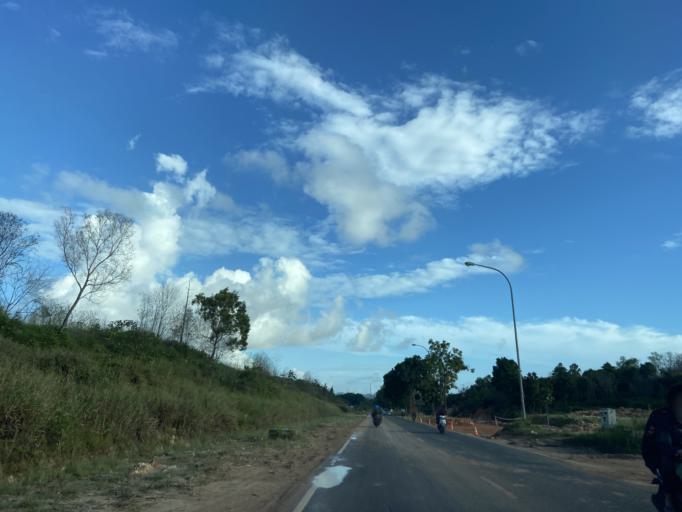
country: SG
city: Singapore
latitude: 1.0200
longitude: 104.0140
